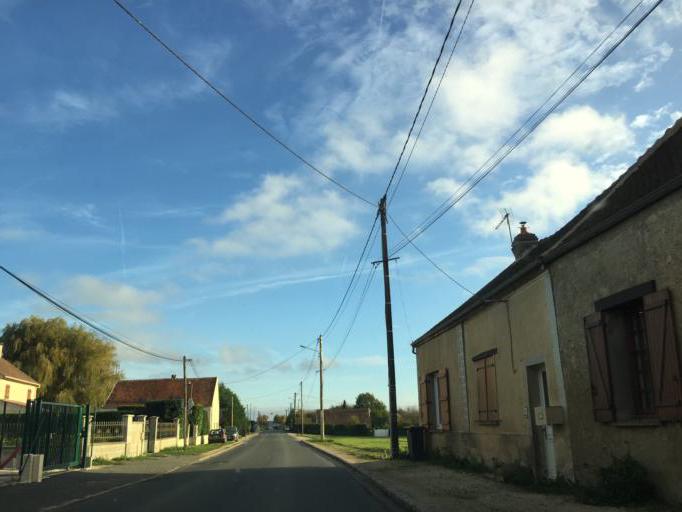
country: FR
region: Ile-de-France
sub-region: Departement de Seine-et-Marne
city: Donnemarie-Dontilly
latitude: 48.5391
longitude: 3.1674
